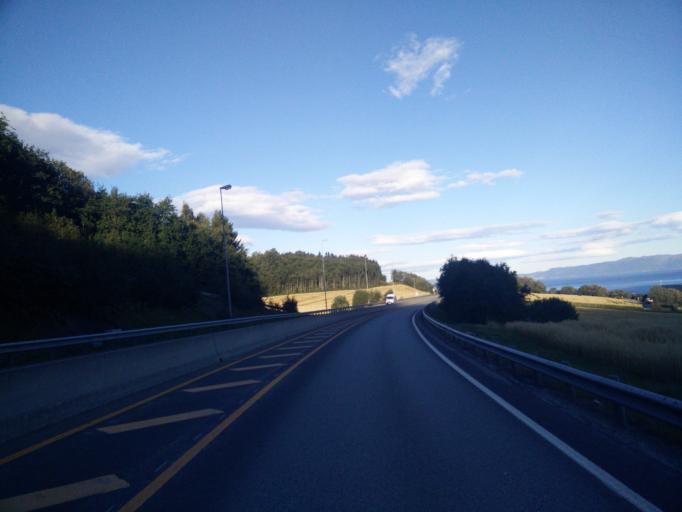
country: NO
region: Sor-Trondelag
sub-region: Malvik
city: Malvik
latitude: 63.4238
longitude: 10.5792
